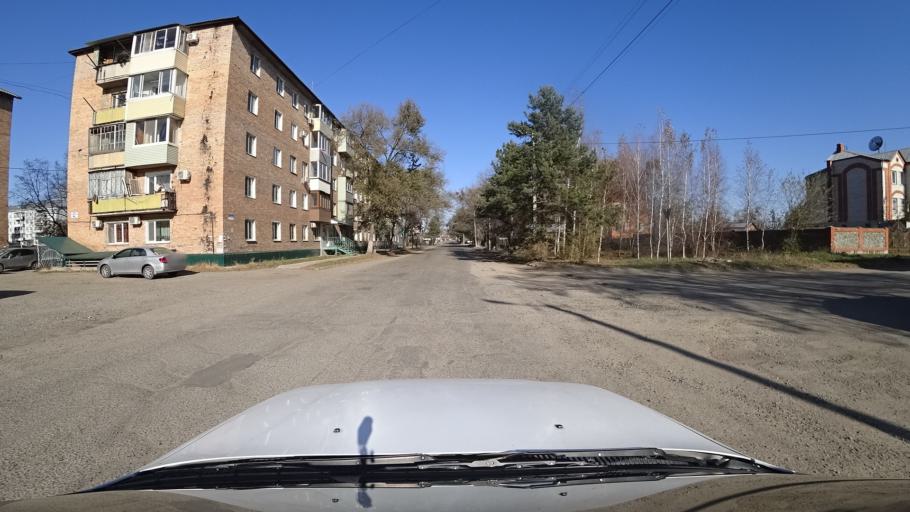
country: RU
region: Primorskiy
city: Dal'nerechensk
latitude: 45.9362
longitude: 133.7331
